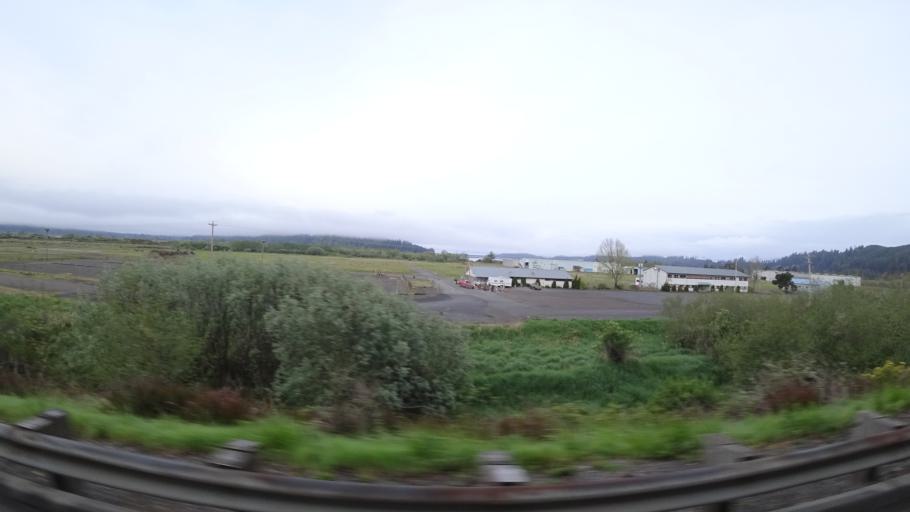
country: US
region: Oregon
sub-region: Douglas County
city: Reedsport
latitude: 43.7446
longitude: -124.1146
